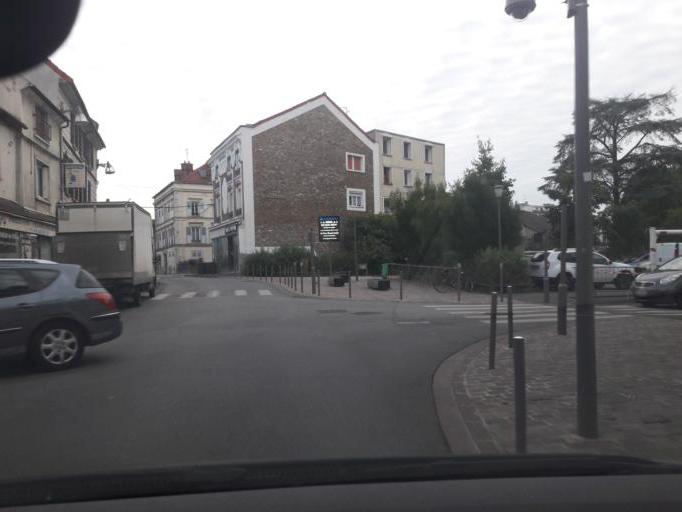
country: FR
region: Ile-de-France
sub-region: Departement de l'Essonne
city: Longjumeau
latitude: 48.6949
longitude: 2.2943
